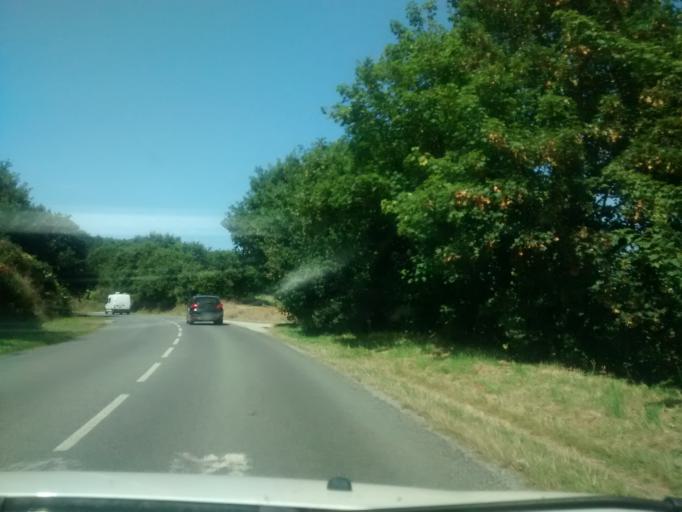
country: FR
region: Brittany
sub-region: Departement d'Ille-et-Vilaine
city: Cancale
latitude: 48.6915
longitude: -1.8482
